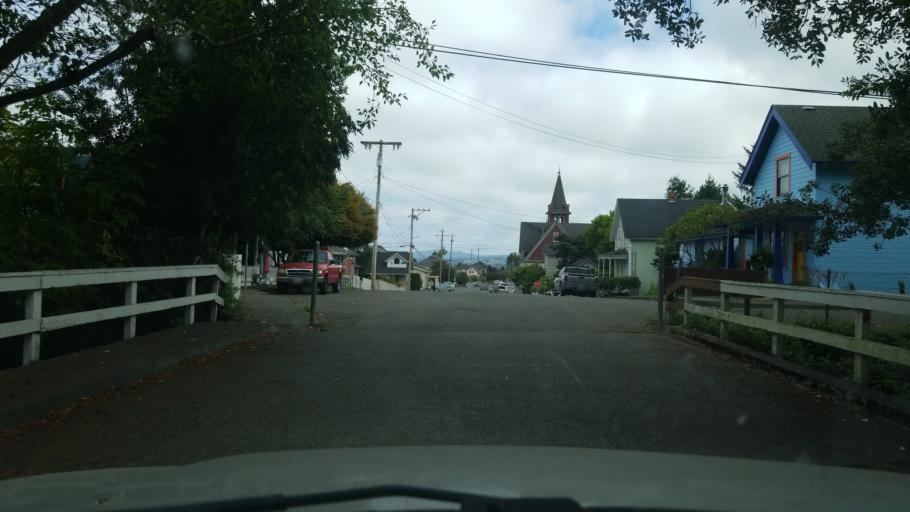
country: US
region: California
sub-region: Humboldt County
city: Ferndale
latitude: 40.5737
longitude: -124.2652
